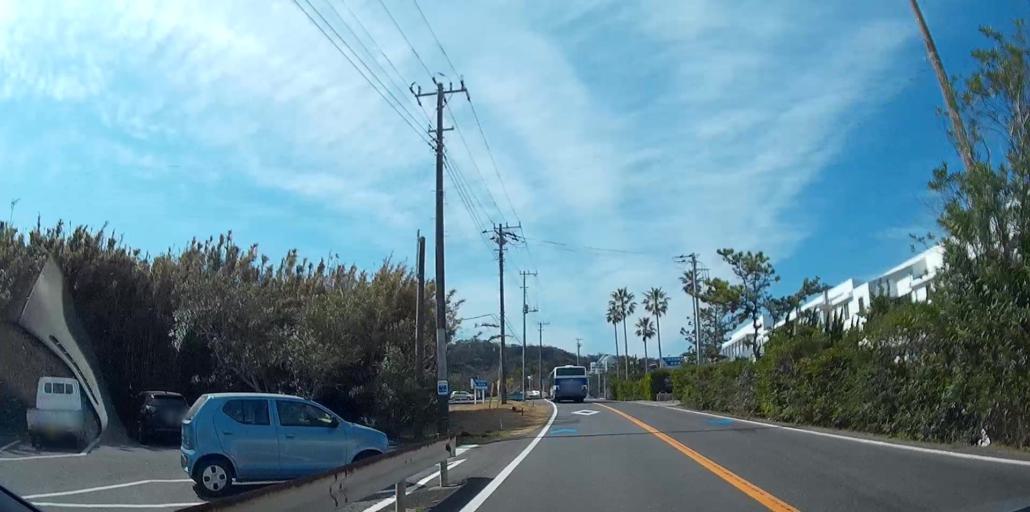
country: JP
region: Chiba
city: Tateyama
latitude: 34.9731
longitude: 139.7931
